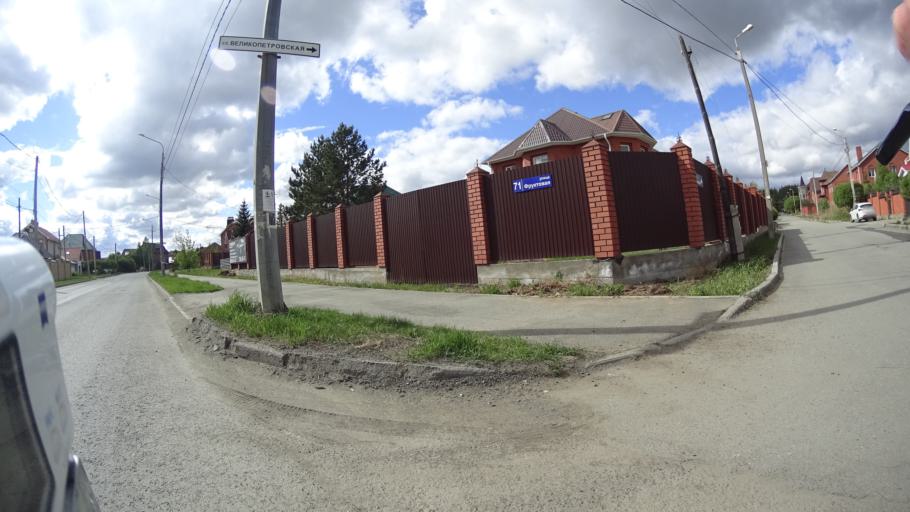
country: RU
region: Chelyabinsk
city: Sargazy
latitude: 55.1522
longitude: 61.2588
